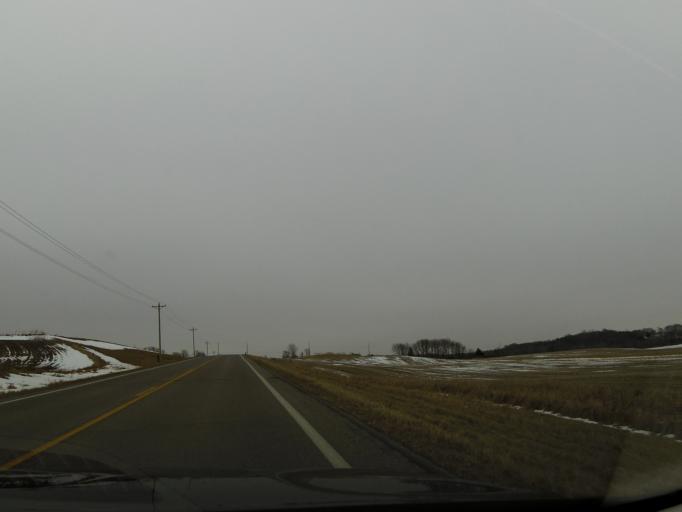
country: US
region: Minnesota
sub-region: Scott County
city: Jordan
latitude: 44.6306
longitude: -93.5697
